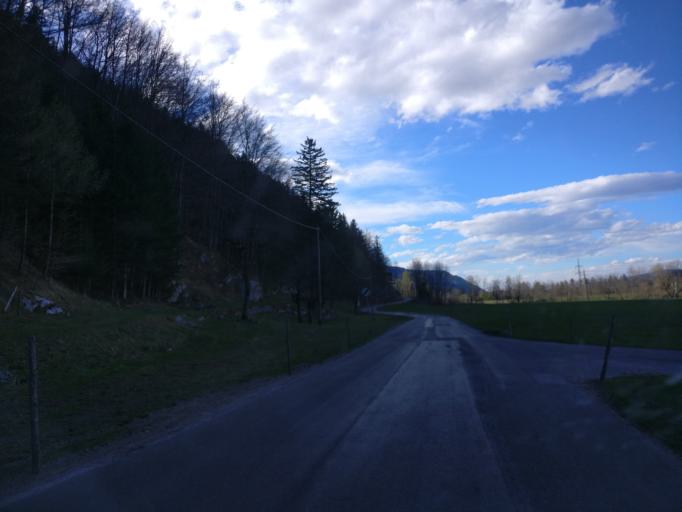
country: AT
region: Salzburg
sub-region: Politischer Bezirk Hallein
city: Golling an der Salzach
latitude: 47.5784
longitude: 13.1739
